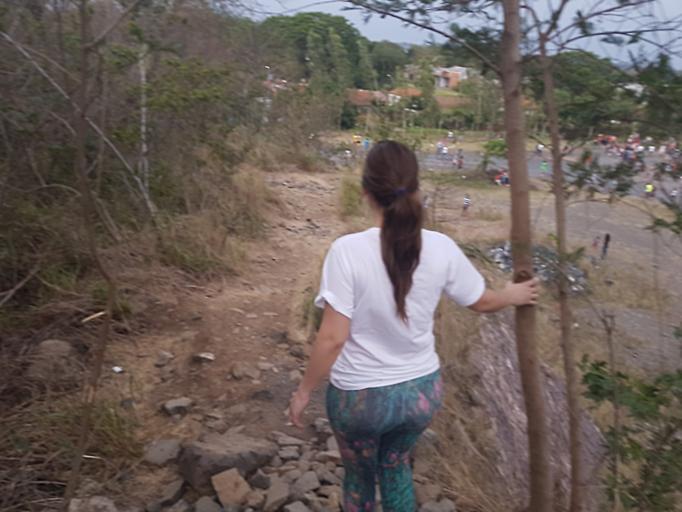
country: PY
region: Central
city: Nemby
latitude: -25.4023
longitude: -57.5367
